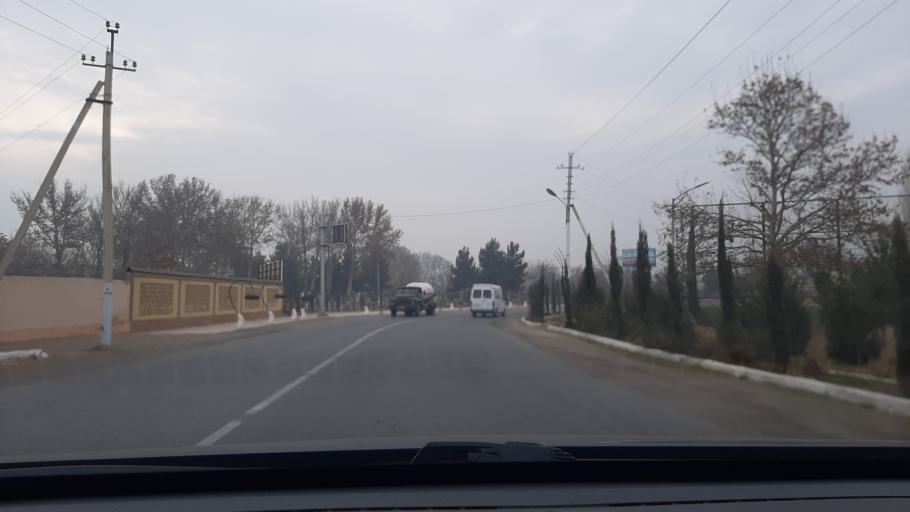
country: TJ
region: Viloyati Sughd
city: Palos
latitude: 40.2716
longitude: 69.8128
